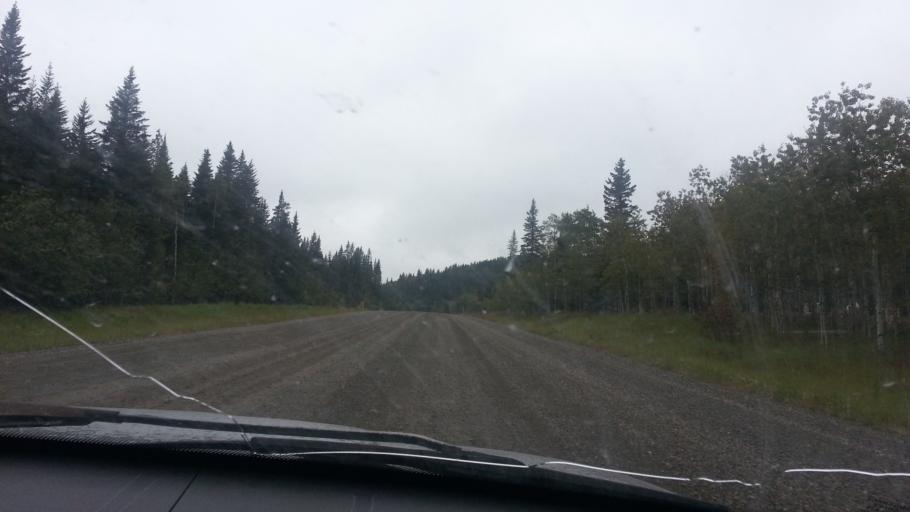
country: CA
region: Alberta
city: Cochrane
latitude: 51.0386
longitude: -114.7340
